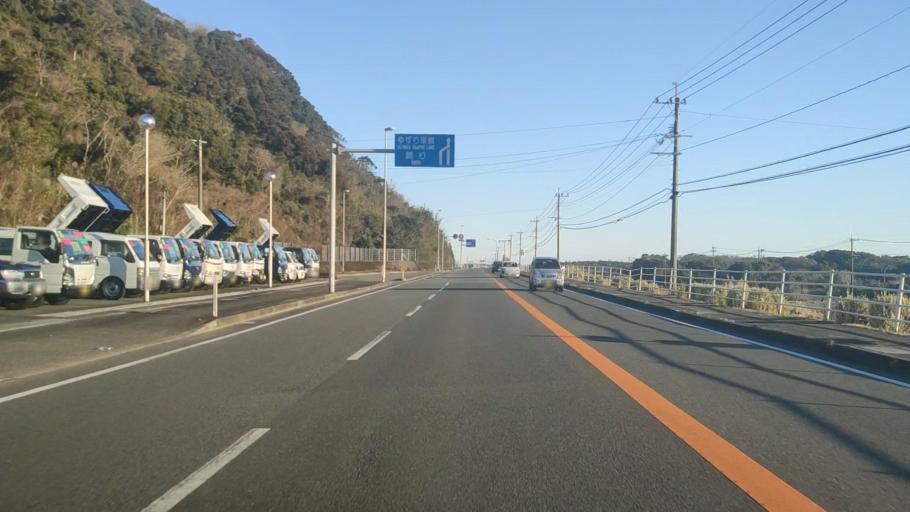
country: JP
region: Miyazaki
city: Takanabe
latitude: 32.1106
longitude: 131.5264
